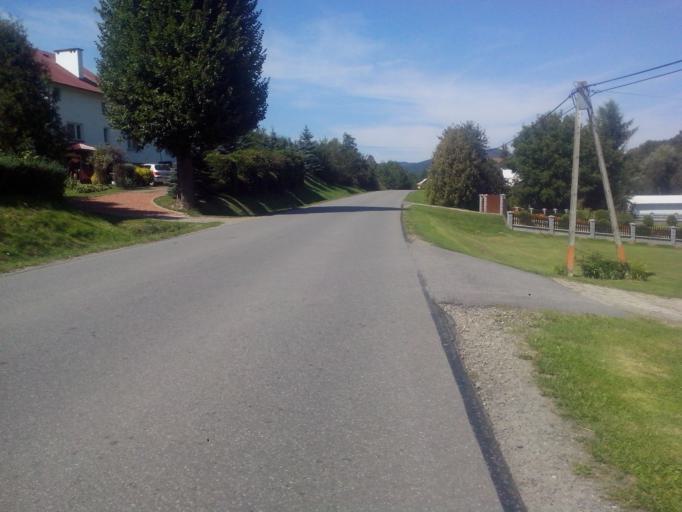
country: PL
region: Subcarpathian Voivodeship
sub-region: Powiat strzyzowski
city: Frysztak
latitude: 49.8666
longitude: 21.6105
